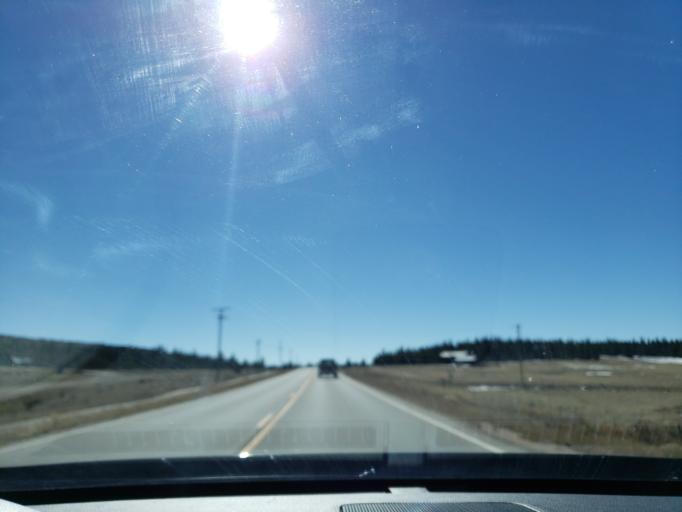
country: US
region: Colorado
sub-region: Park County
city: Fairplay
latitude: 39.2612
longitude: -106.0419
